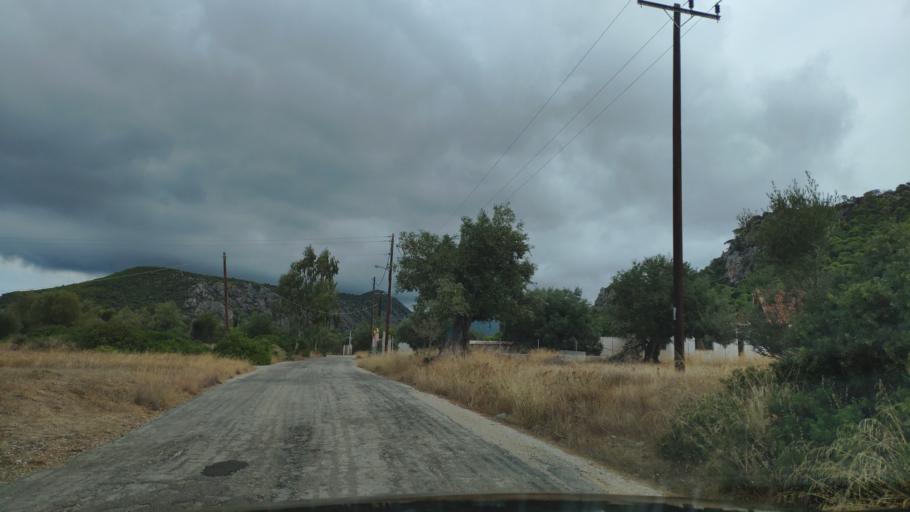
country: GR
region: Peloponnese
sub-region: Nomos Korinthias
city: Vrakhati
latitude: 38.0298
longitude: 22.8588
